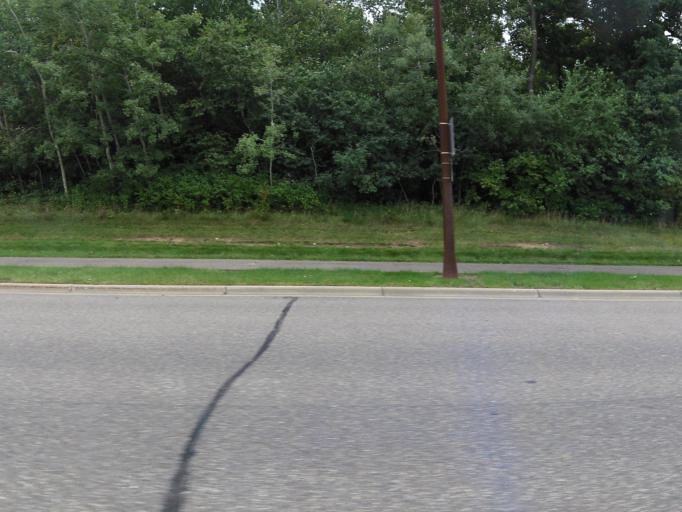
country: US
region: Minnesota
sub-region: Dakota County
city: Inver Grove Heights
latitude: 44.8206
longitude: -93.0369
